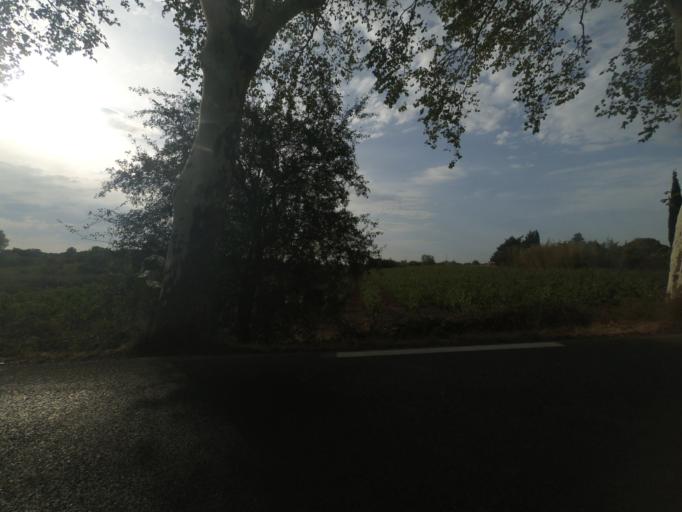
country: FR
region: Languedoc-Roussillon
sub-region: Departement de l'Herault
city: Restinclieres
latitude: 43.7291
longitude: 4.0434
